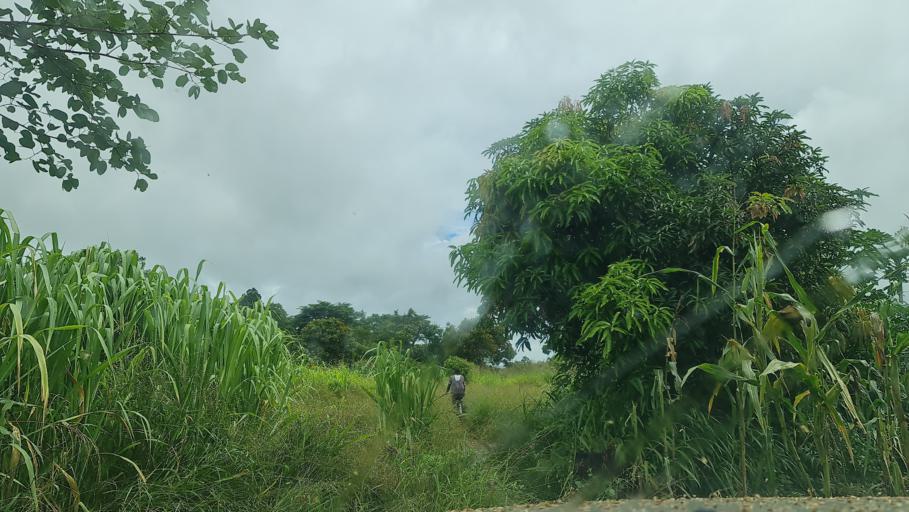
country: MW
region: Southern Region
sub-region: Nsanje District
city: Nsanje
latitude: -17.4455
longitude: 35.8443
